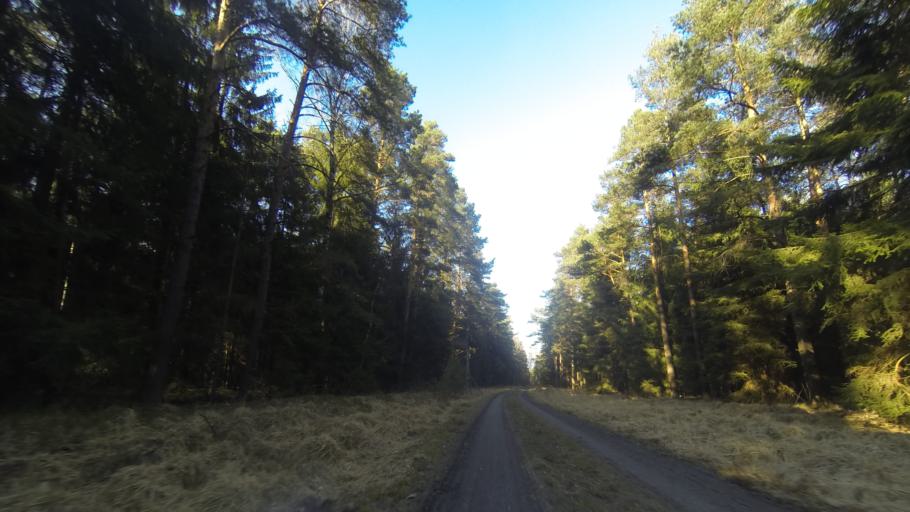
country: DE
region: Saxony
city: Laussnitz
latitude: 51.2561
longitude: 13.8456
